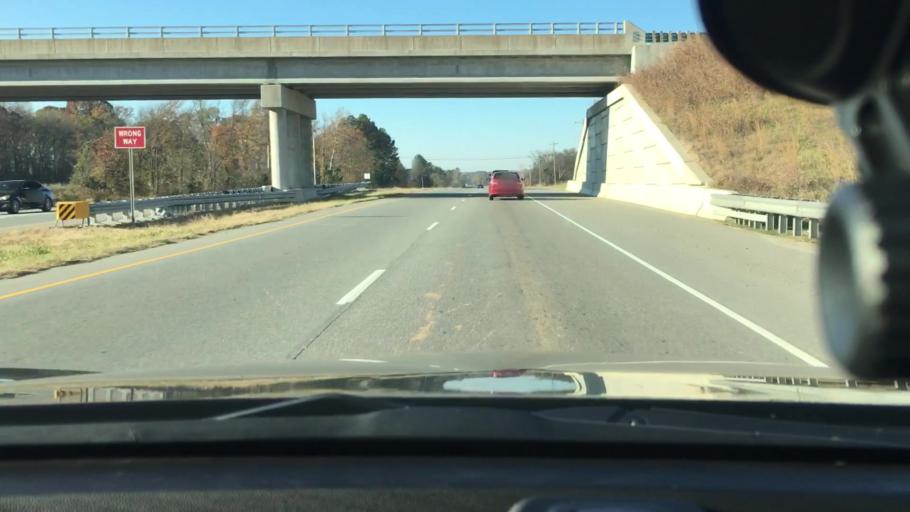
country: US
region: North Carolina
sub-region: Cabarrus County
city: Harrisburg
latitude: 35.3372
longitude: -80.6194
